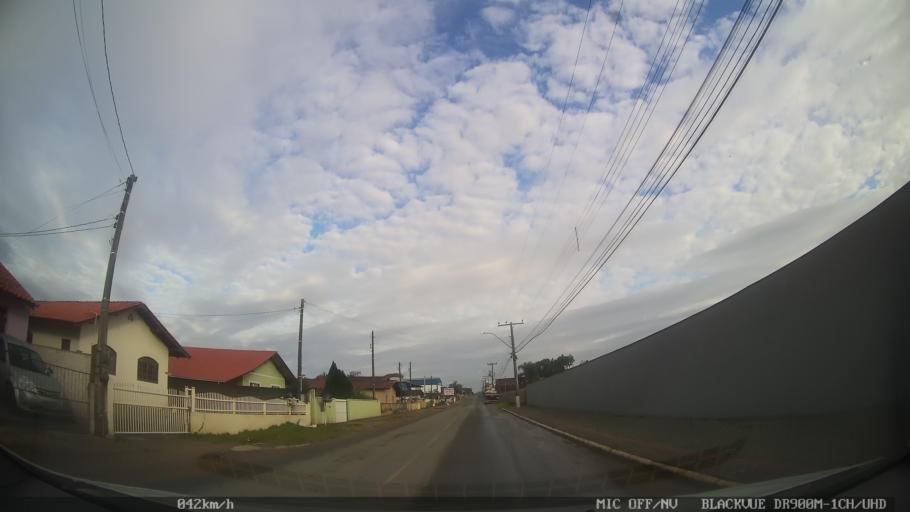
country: BR
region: Santa Catarina
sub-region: Barra Velha
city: Barra Velha
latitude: -26.6206
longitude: -48.7111
